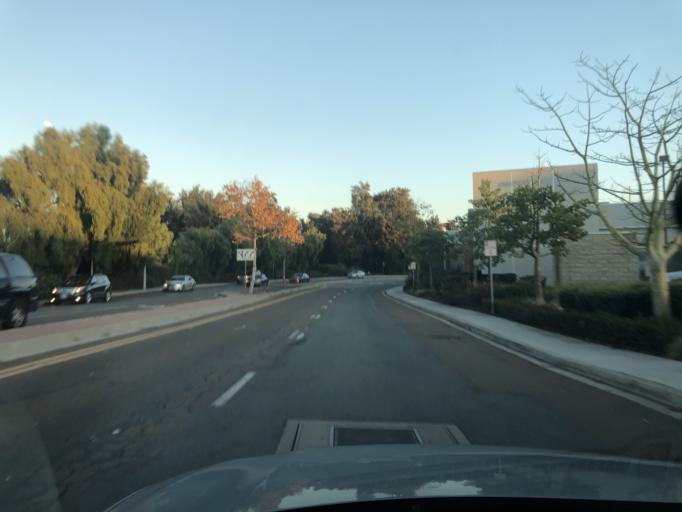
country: US
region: California
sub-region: San Diego County
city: Chula Vista
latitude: 32.6488
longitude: -117.0593
